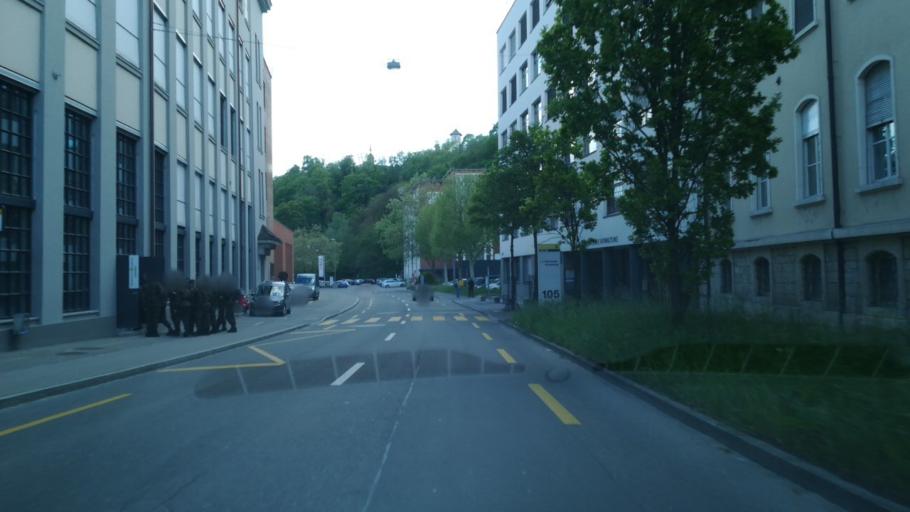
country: CH
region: Schaffhausen
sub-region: Bezirk Schaffhausen
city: Schaffhausen
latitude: 47.7047
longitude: 8.6300
